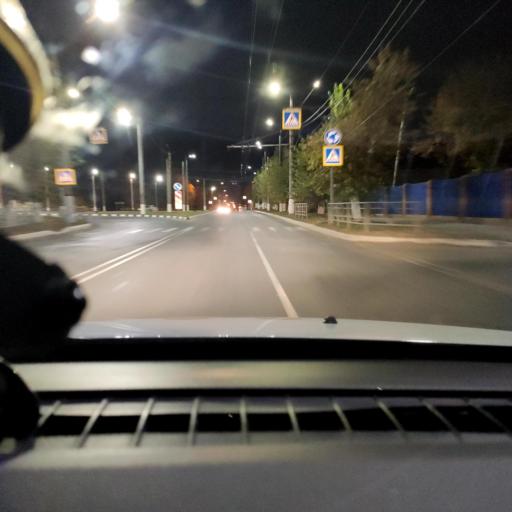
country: RU
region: Samara
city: Novokuybyshevsk
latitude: 53.1021
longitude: 49.9408
